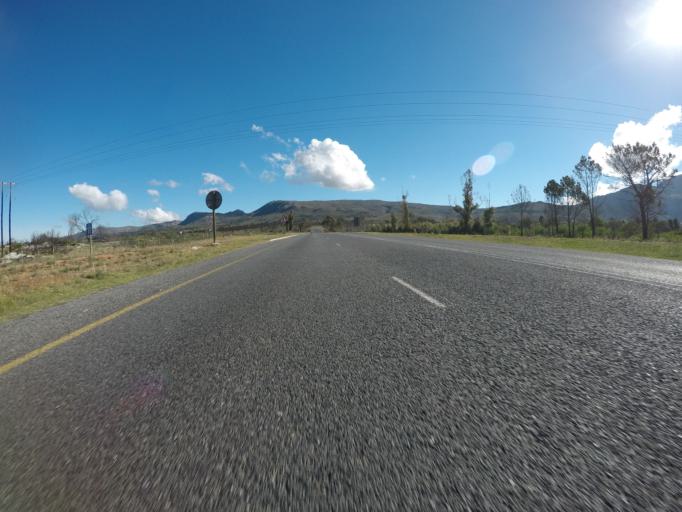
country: ZA
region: Western Cape
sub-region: Overberg District Municipality
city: Hermanus
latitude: -34.2351
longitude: 19.2002
